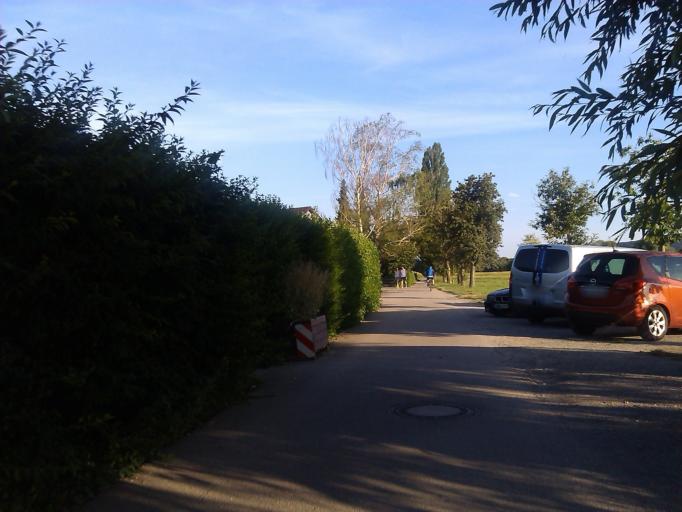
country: DE
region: Baden-Wuerttemberg
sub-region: Karlsruhe Region
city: Wiesloch
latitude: 49.2832
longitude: 8.6931
